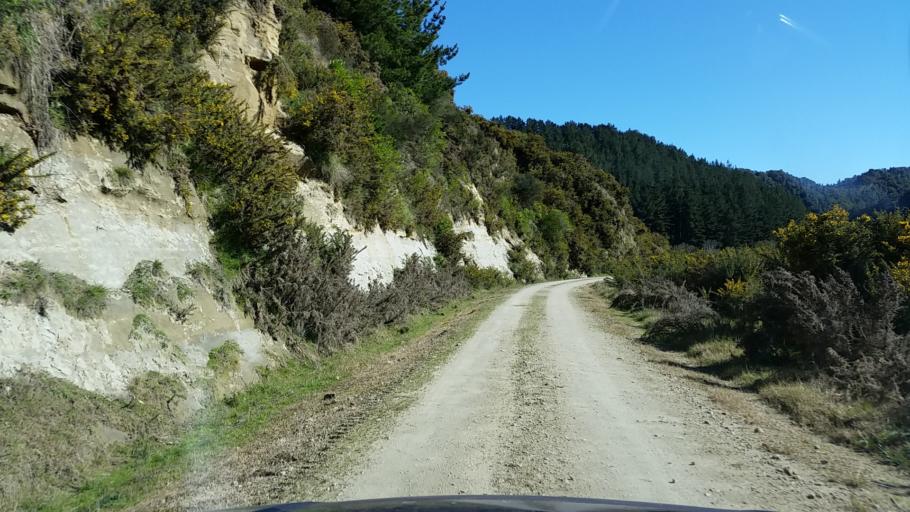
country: NZ
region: Manawatu-Wanganui
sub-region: Wanganui District
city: Wanganui
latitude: -39.6681
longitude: 174.8696
